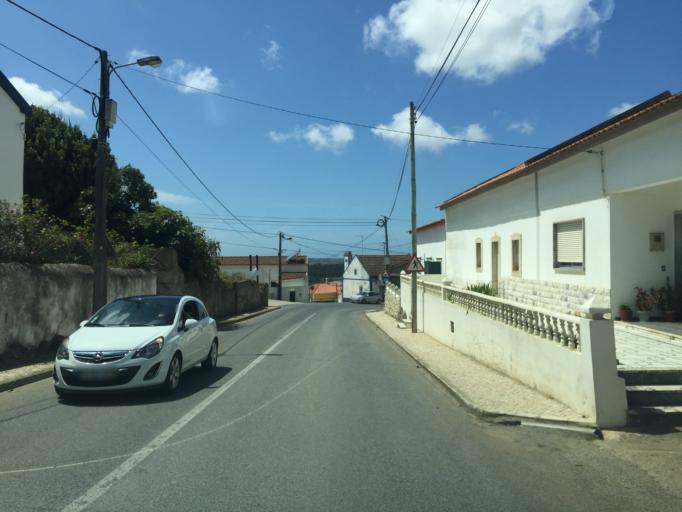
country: PT
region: Lisbon
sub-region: Lourinha
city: Lourinha
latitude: 39.2754
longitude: -9.2781
